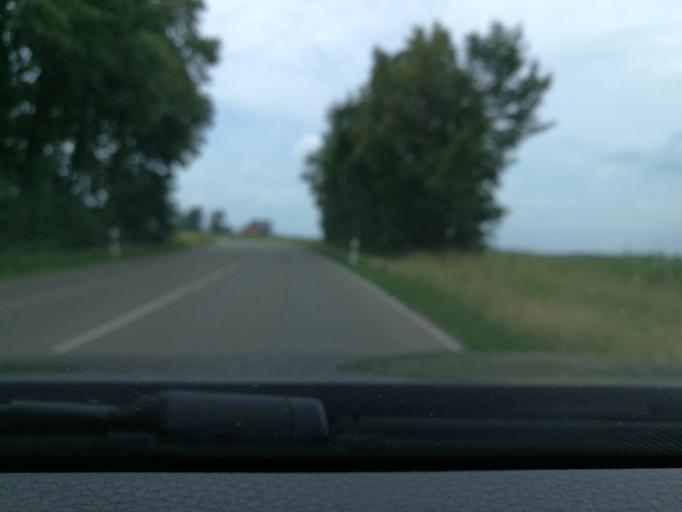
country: DE
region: Bavaria
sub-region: Regierungsbezirk Mittelfranken
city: Seukendorf
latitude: 49.4883
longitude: 10.8999
